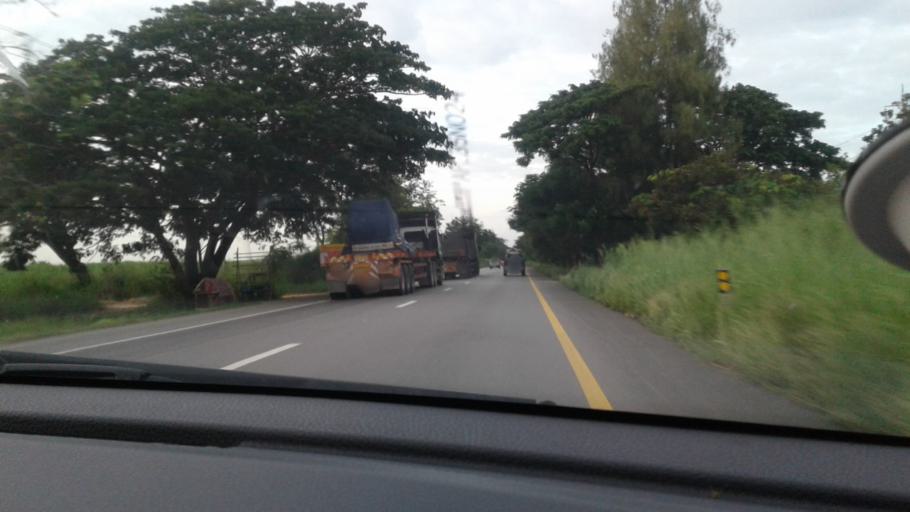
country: TH
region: Prachuap Khiri Khan
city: Hua Hin
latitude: 12.5441
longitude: 99.8748
